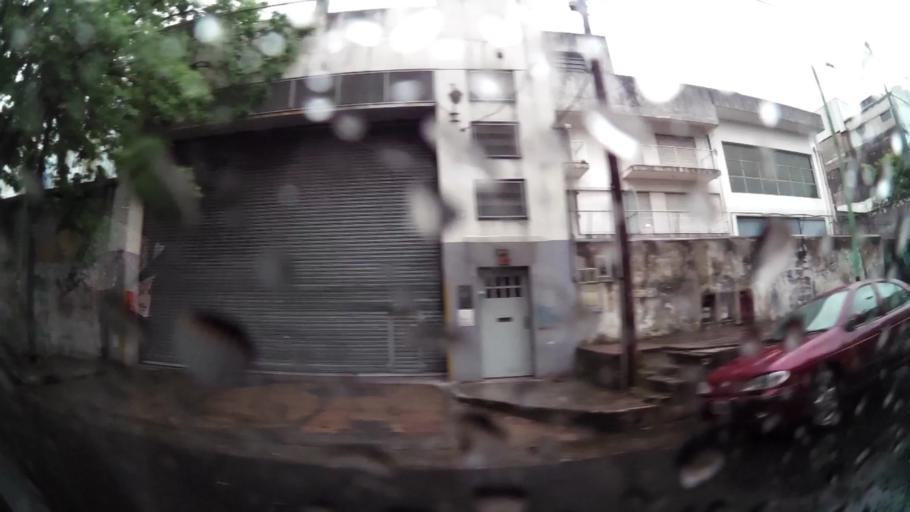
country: AR
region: Buenos Aires
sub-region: Partido de Avellaneda
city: Avellaneda
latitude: -34.6441
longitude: -58.3656
